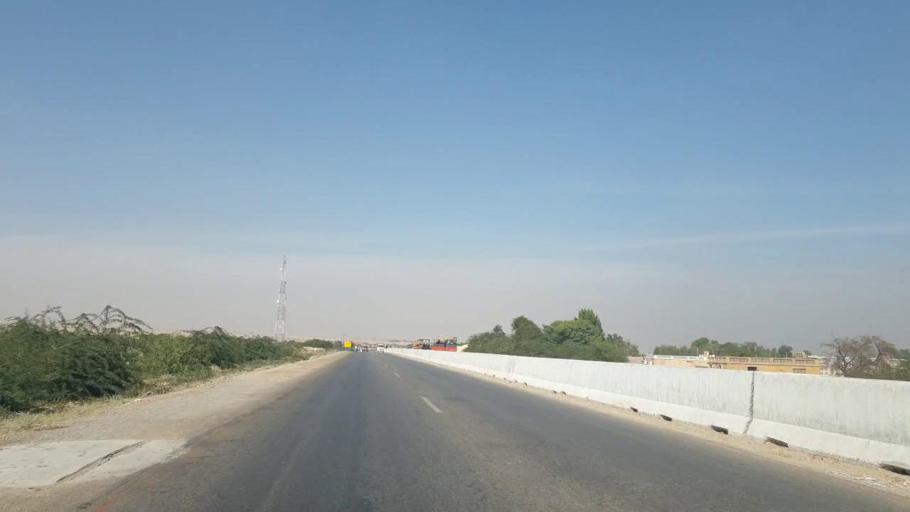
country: PK
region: Sindh
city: Hala
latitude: 25.7150
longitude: 68.2954
